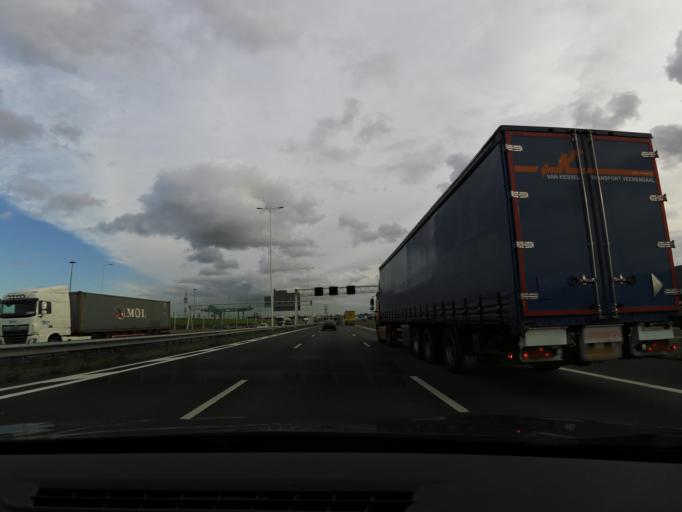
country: NL
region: South Holland
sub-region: Gemeente Albrandswaard
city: Rhoon
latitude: 51.8724
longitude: 4.4192
